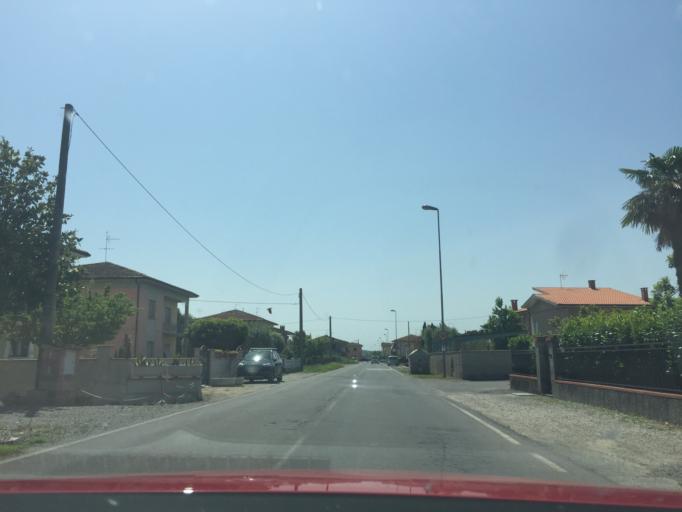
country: IT
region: Tuscany
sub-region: Provincia di Pistoia
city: Anchione
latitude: 43.8319
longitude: 10.7540
